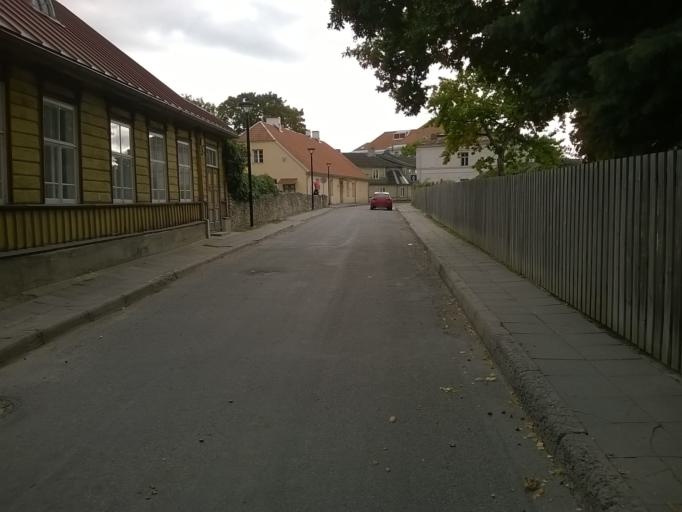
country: EE
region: Laeaene
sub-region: Haapsalu linn
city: Haapsalu
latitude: 58.9481
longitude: 23.5348
